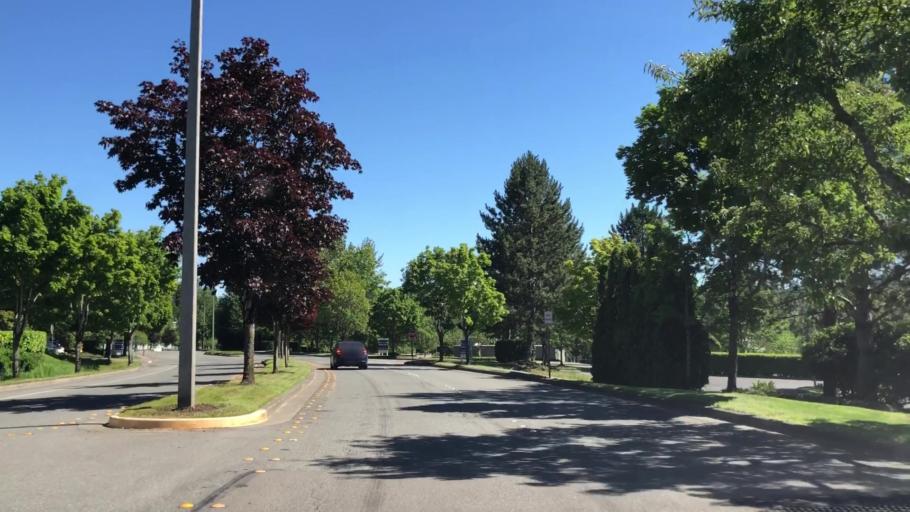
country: US
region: Washington
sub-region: Snohomish County
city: North Creek
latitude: 47.7969
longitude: -122.1982
